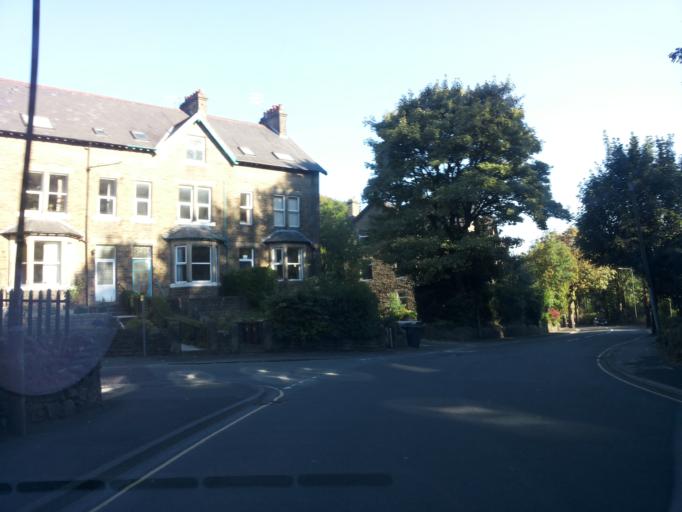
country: GB
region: England
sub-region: Derbyshire
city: Buxton
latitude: 53.2549
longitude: -1.9088
